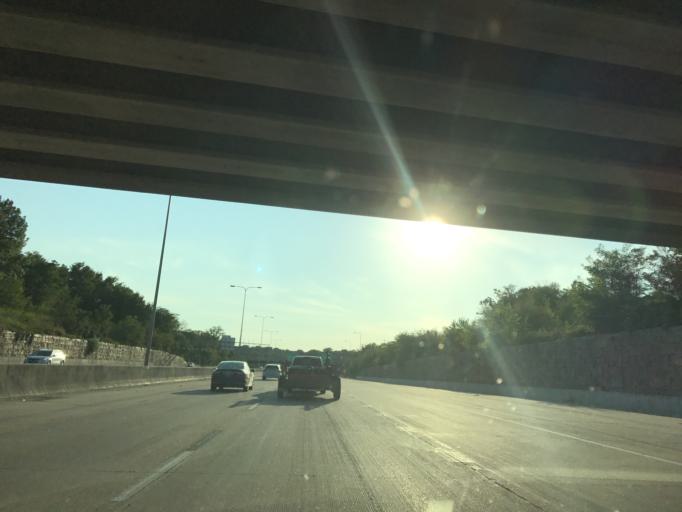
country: US
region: Nebraska
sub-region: Douglas County
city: Omaha
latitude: 41.2309
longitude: -95.9237
